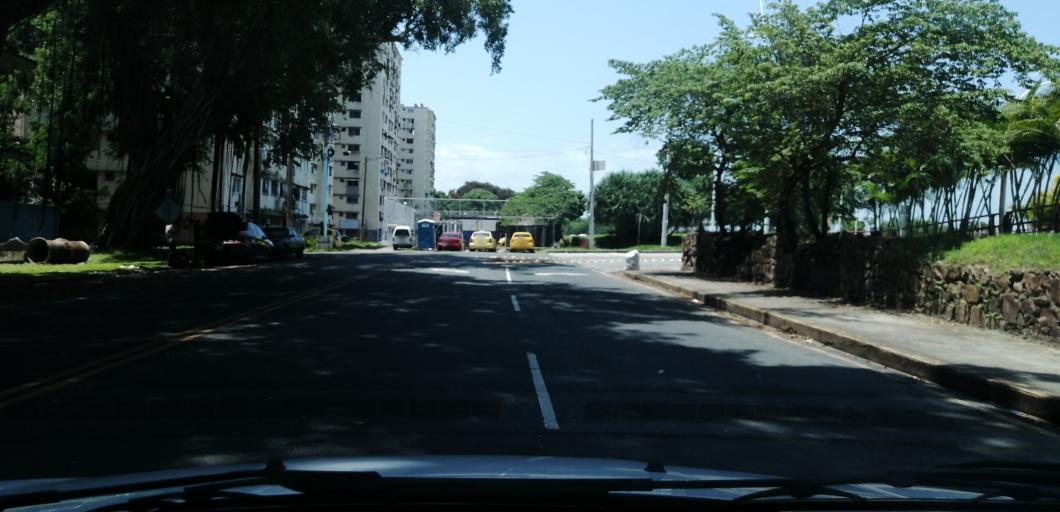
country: PA
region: Panama
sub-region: Distrito de Panama
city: Ancon
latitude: 8.9494
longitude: -79.5418
